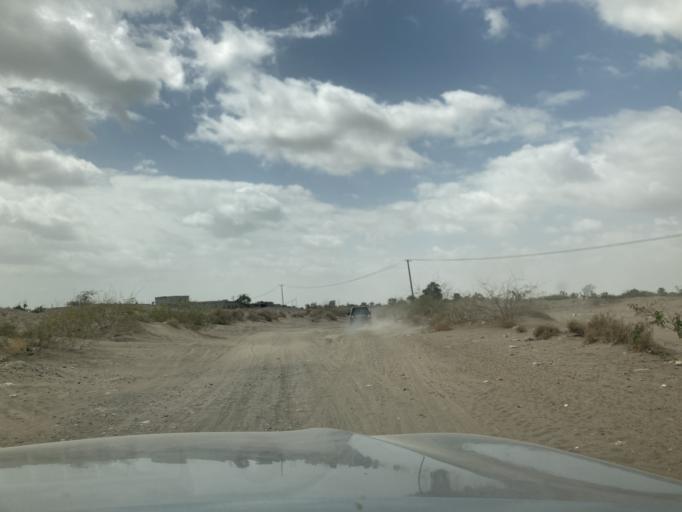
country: YE
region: Lahij
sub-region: Al  Hawtah
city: Lahij
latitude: 13.0213
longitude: 45.0027
